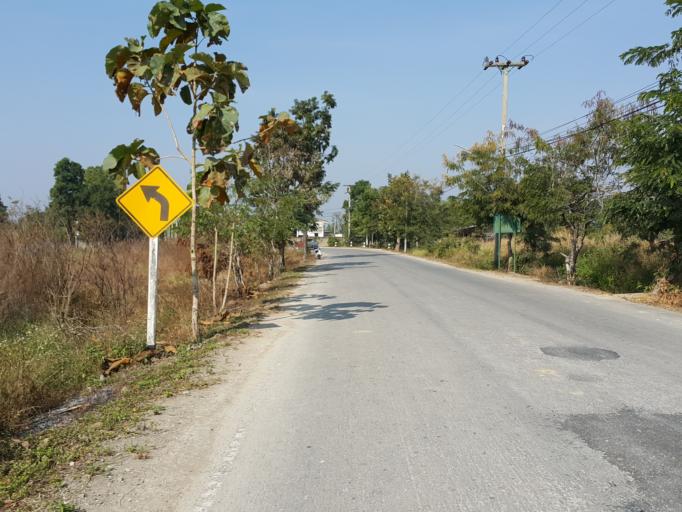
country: TH
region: Lamphun
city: Ban Thi
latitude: 18.6515
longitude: 99.0711
